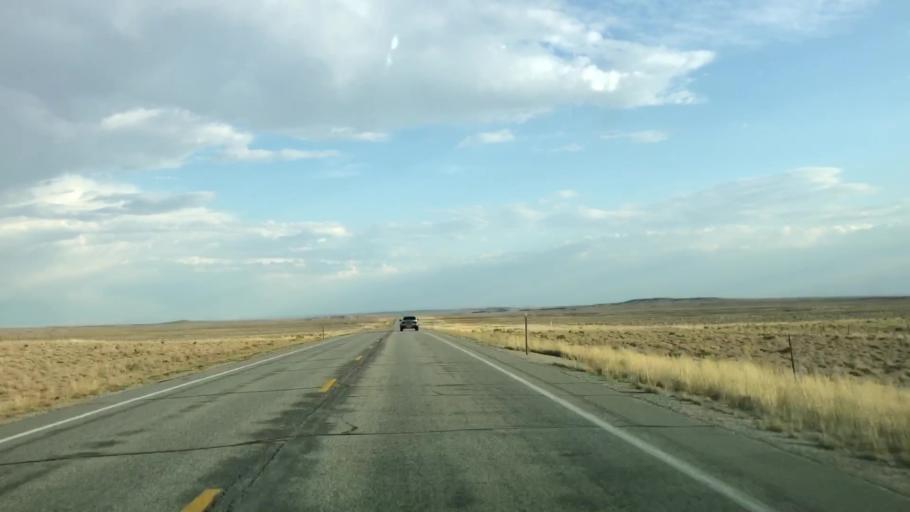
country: US
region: Wyoming
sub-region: Sublette County
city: Pinedale
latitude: 42.3878
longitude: -109.5387
